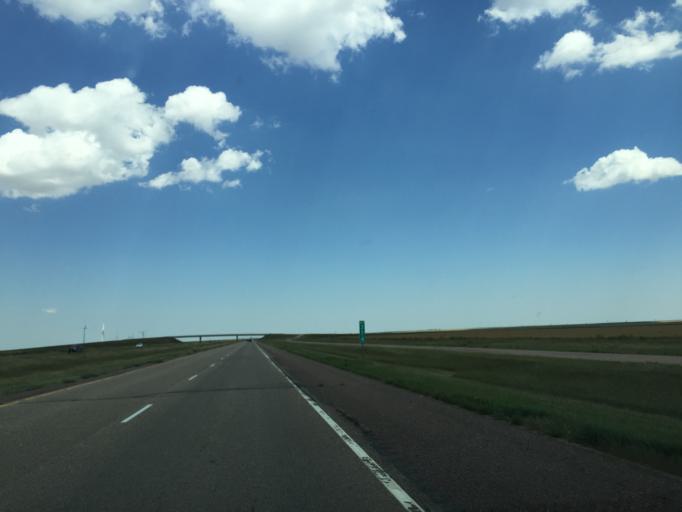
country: US
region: Colorado
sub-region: Lincoln County
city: Hugo
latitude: 39.2777
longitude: -103.4449
